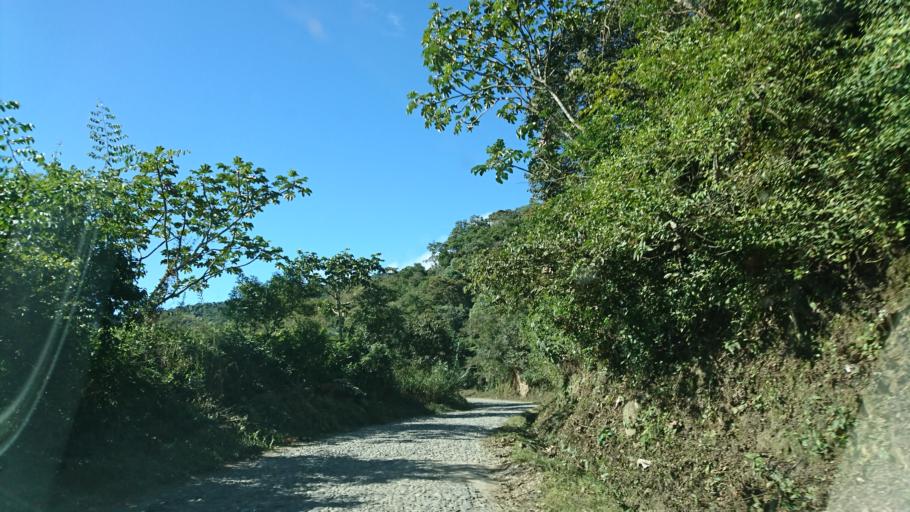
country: BO
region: La Paz
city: Coroico
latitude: -16.2175
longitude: -67.7378
